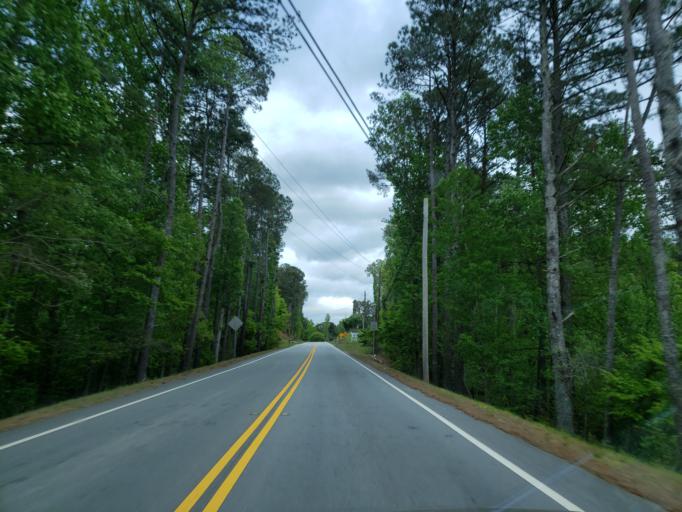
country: US
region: Georgia
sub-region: Paulding County
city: Dallas
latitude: 33.8725
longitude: -84.8820
